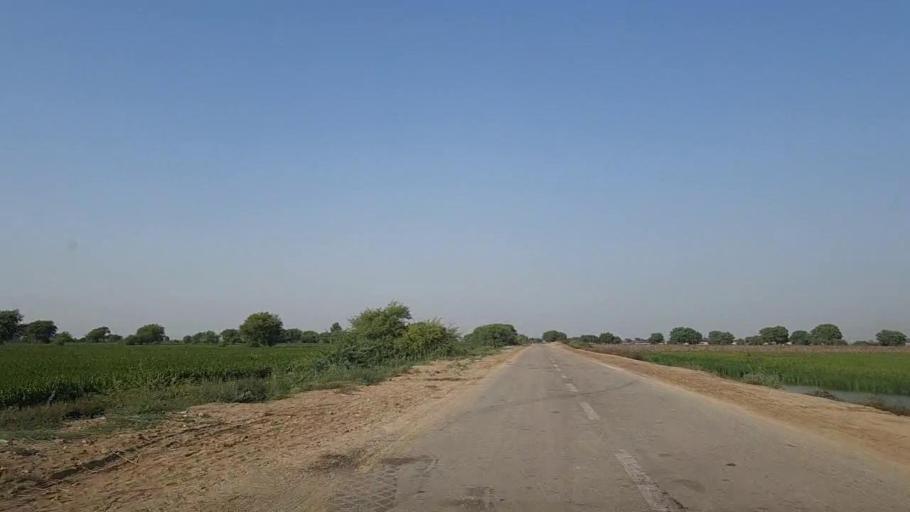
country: PK
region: Sindh
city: Mirpur Batoro
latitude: 24.5742
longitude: 68.3943
